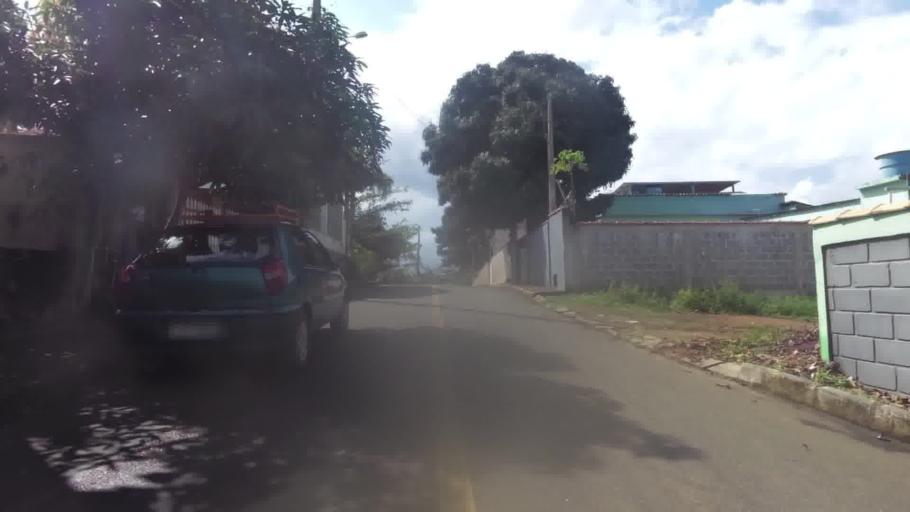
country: BR
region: Espirito Santo
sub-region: Piuma
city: Piuma
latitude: -20.8268
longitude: -40.6948
